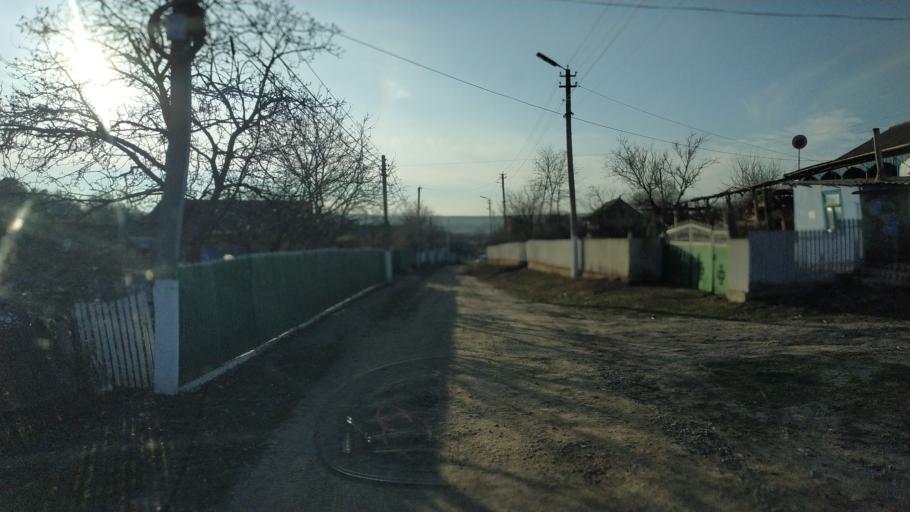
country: MD
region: Hincesti
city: Hincesti
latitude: 46.6994
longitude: 28.5367
